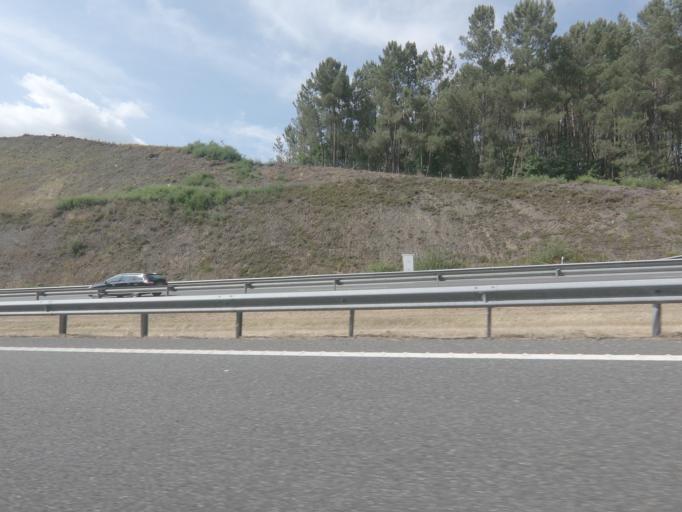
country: ES
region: Galicia
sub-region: Provincia de Ourense
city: Beade
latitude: 42.3080
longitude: -8.1081
